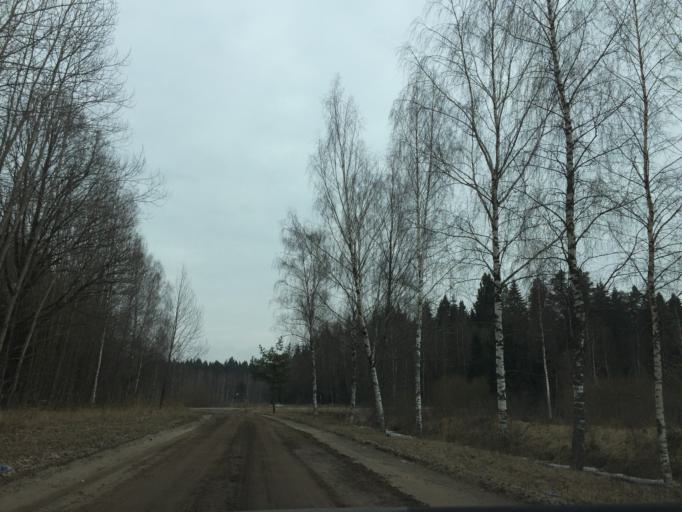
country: LV
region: Kekava
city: Balozi
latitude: 56.7775
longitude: 24.1286
